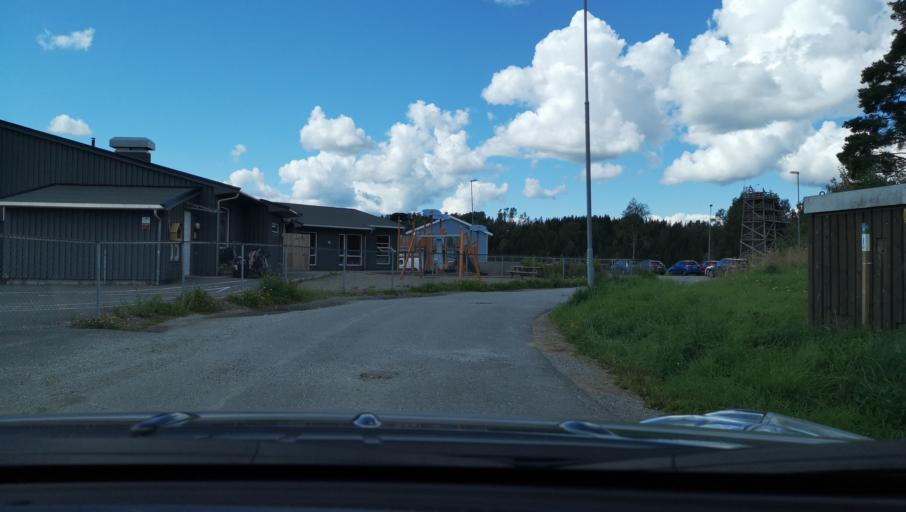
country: NO
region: Ostfold
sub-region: Hobol
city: Tomter
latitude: 59.6649
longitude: 10.9986
